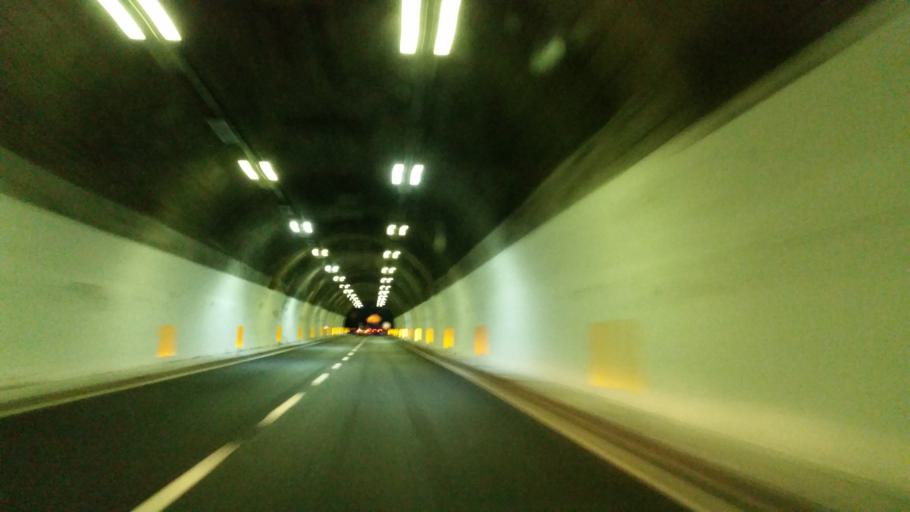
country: IT
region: Liguria
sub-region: Provincia di Imperia
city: Diano Marina
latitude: 43.9109
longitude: 8.0685
